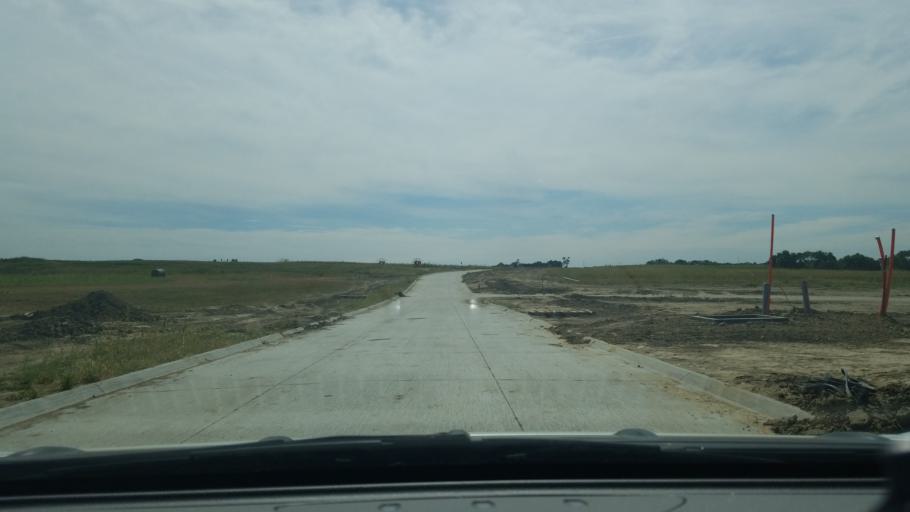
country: US
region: Nebraska
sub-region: Sarpy County
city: Chalco
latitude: 41.1447
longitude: -96.1096
